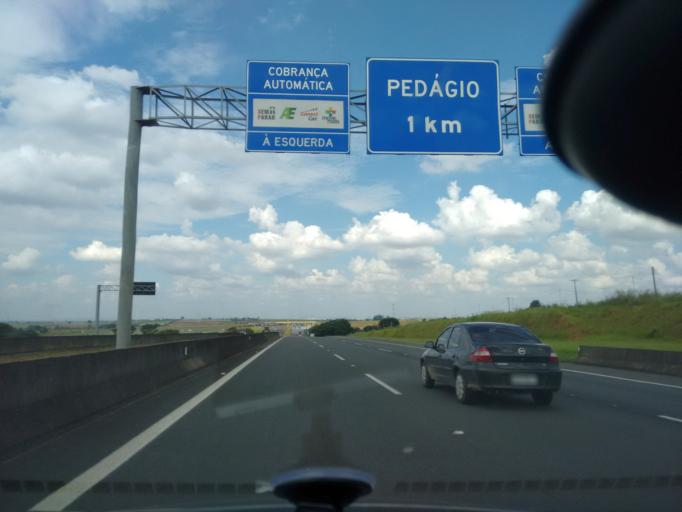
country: BR
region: Sao Paulo
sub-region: Sumare
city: Sumare
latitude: -22.8555
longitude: -47.3107
